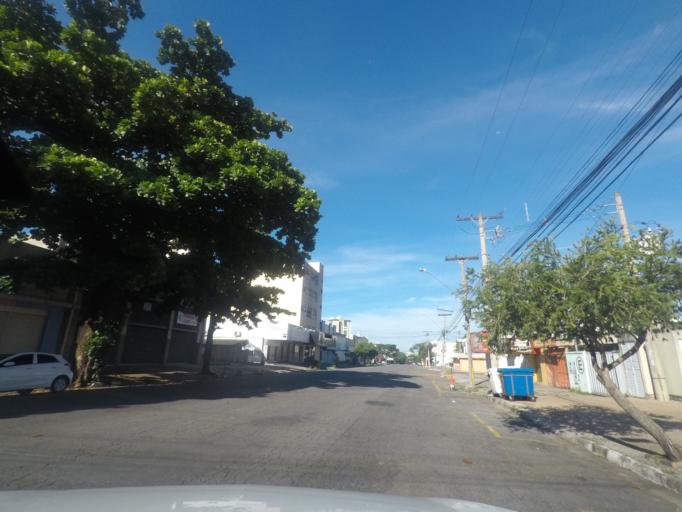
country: BR
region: Goias
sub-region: Goiania
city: Goiania
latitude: -16.6773
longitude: -49.2688
